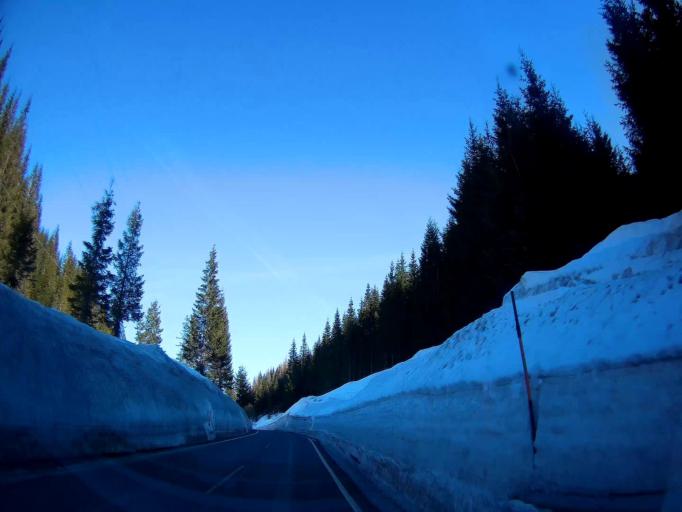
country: AT
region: Salzburg
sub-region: Politischer Bezirk Zell am See
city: Dienten am Hochkonig
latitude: 47.3976
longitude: 12.9986
